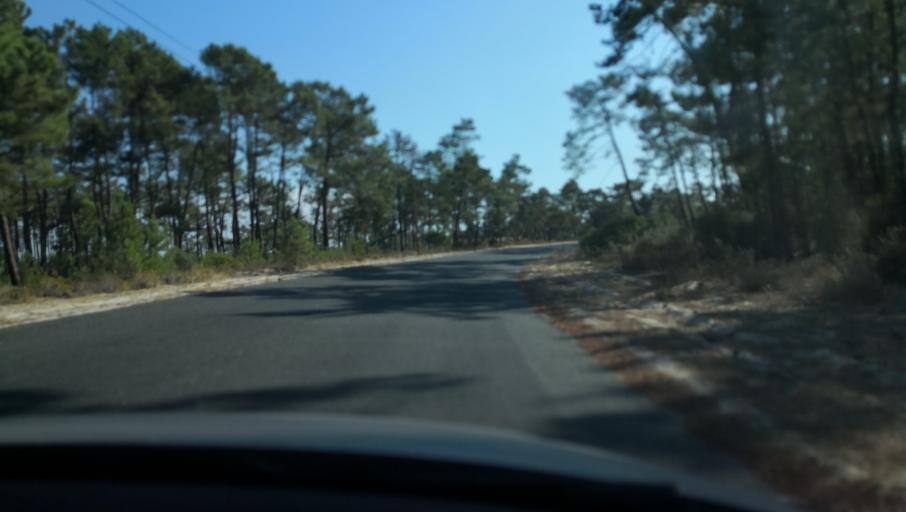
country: PT
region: Setubal
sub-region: Setubal
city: Setubal
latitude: 38.4678
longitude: -8.8696
